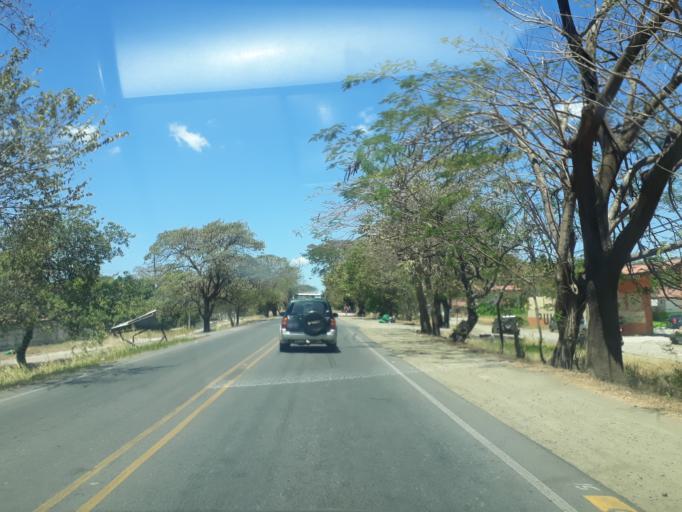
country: CR
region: Guanacaste
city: Liberia
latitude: 10.6551
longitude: -85.4668
